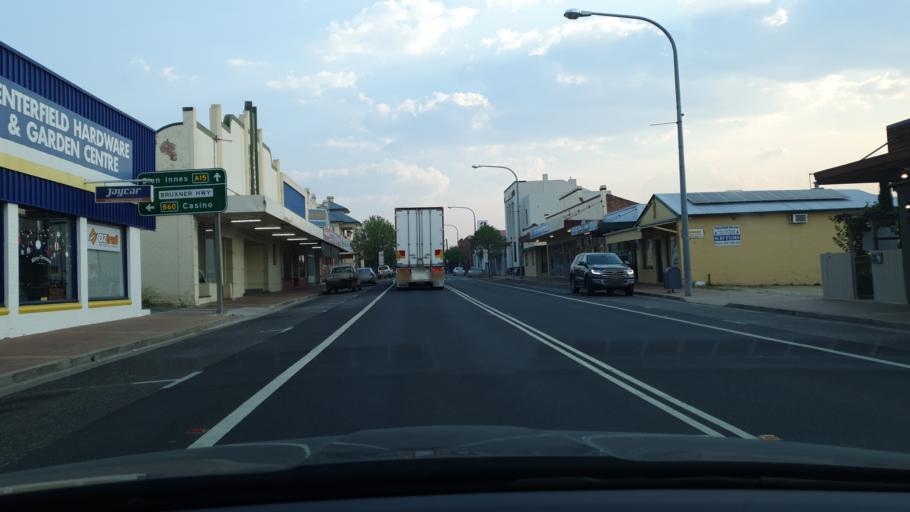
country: AU
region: New South Wales
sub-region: Tenterfield Municipality
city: Carrolls Creek
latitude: -29.0518
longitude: 152.0195
